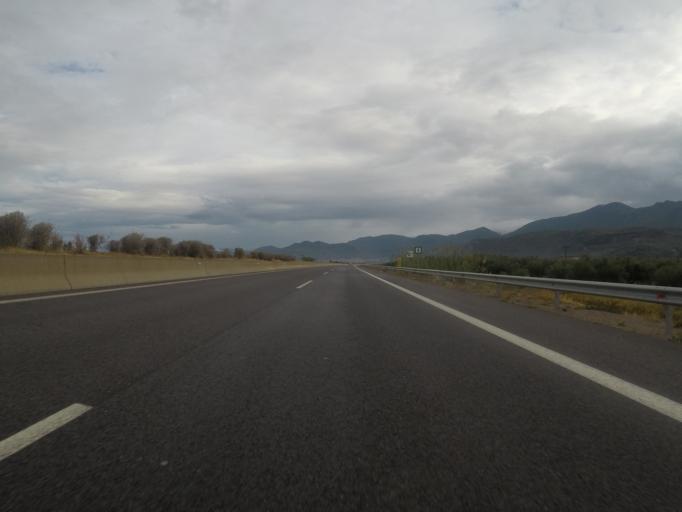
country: GR
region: Peloponnese
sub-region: Nomos Messinias
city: Thouria
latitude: 37.1109
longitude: 22.0346
